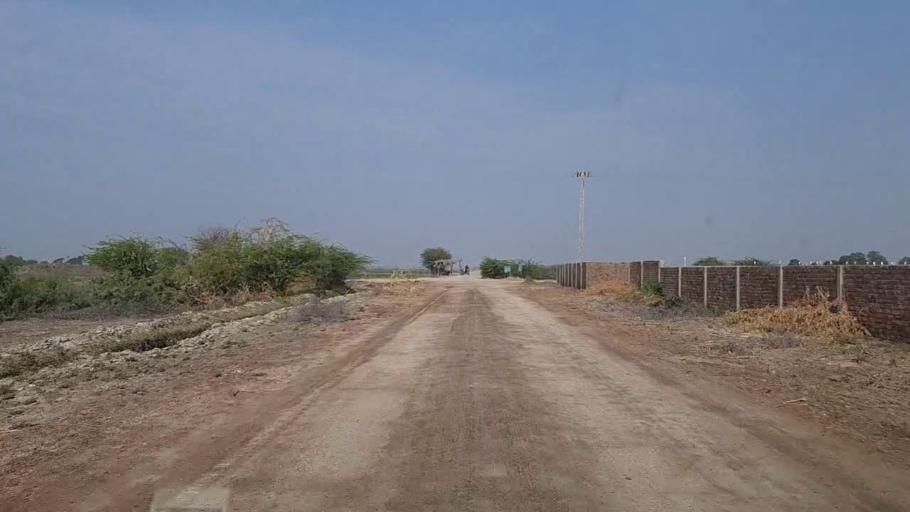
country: PK
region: Sindh
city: Mirwah Gorchani
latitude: 25.3492
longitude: 69.0637
